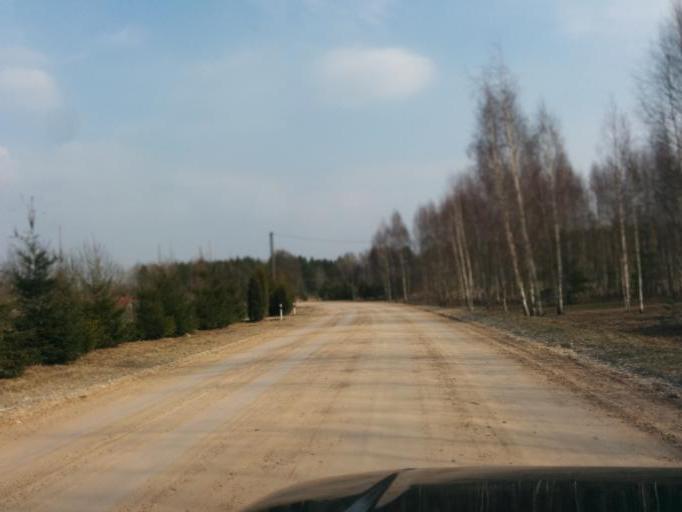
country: LV
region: Olaine
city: Olaine
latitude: 56.7909
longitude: 23.9984
